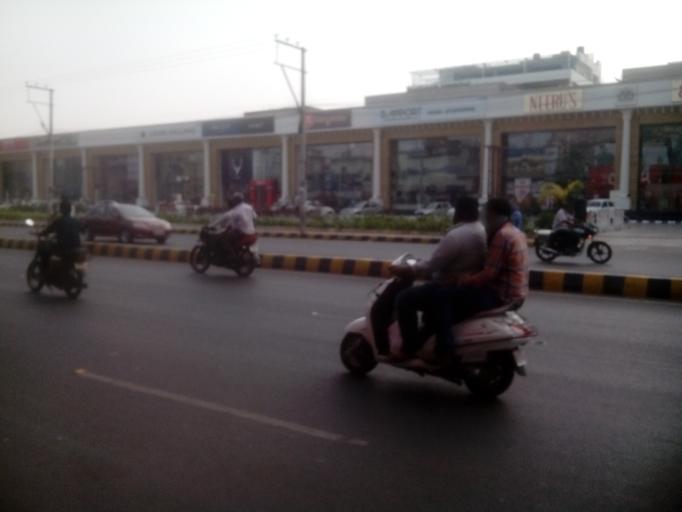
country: IN
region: Andhra Pradesh
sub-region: Krishna
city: Vijayawada
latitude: 16.5015
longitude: 80.6440
